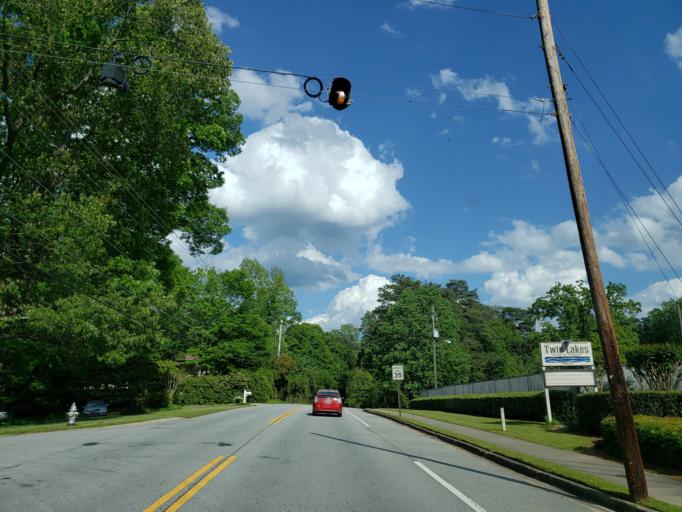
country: US
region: Georgia
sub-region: DeKalb County
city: North Druid Hills
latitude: 33.8464
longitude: -84.2749
